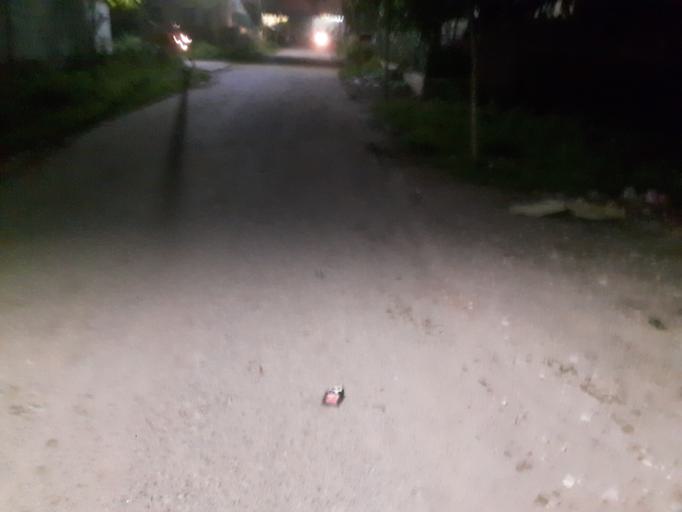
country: IN
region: Telangana
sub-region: Rangareddi
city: Quthbullapur
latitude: 17.4979
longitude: 78.4672
